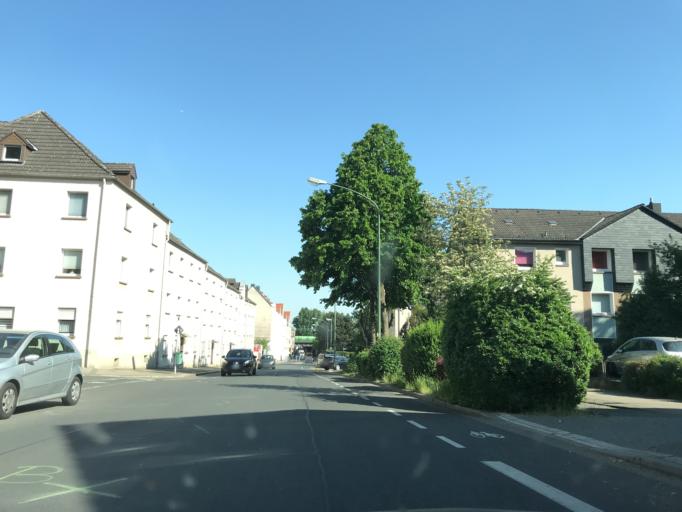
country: DE
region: North Rhine-Westphalia
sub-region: Regierungsbezirk Munster
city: Gelsenkirchen
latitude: 51.4681
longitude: 7.0854
